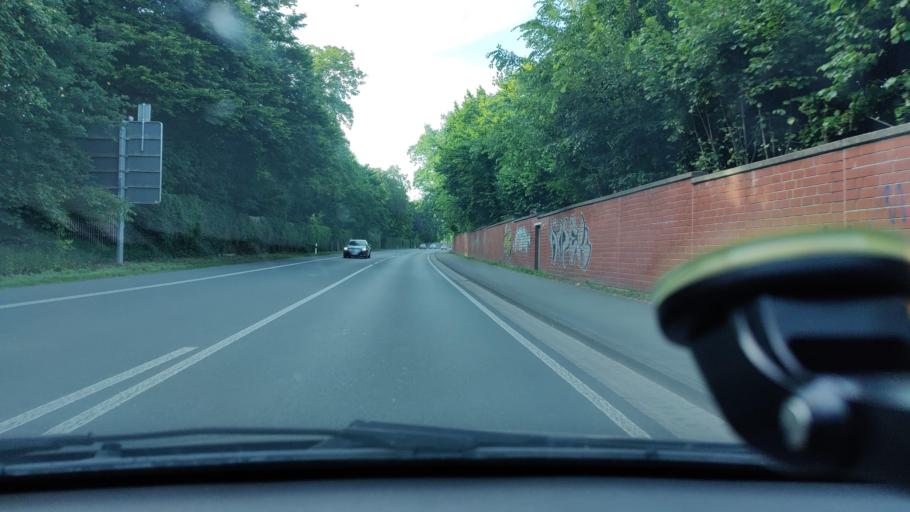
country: DE
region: North Rhine-Westphalia
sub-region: Regierungsbezirk Munster
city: Coesfeld
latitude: 51.9437
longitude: 7.1501
